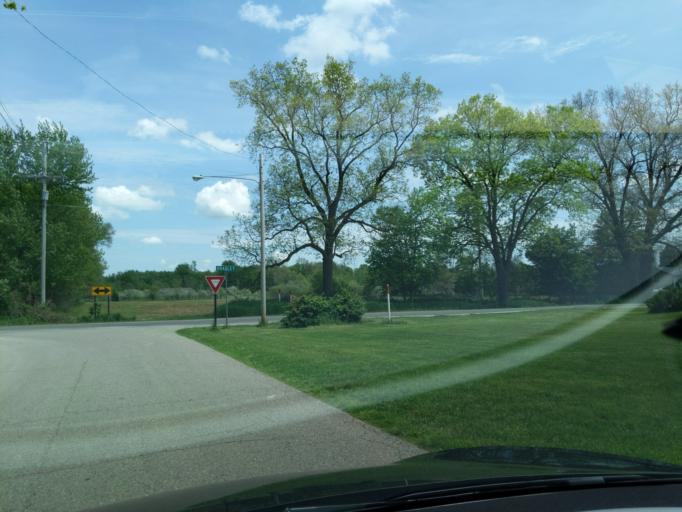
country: US
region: Michigan
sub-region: Ingham County
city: Stockbridge
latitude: 42.4969
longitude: -84.1078
